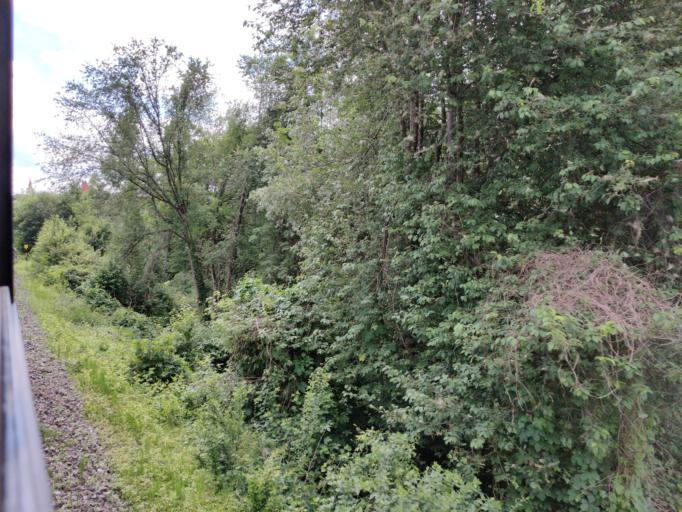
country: AT
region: Styria
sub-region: Politischer Bezirk Leibnitz
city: Spielfeld
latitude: 46.7136
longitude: 15.6297
